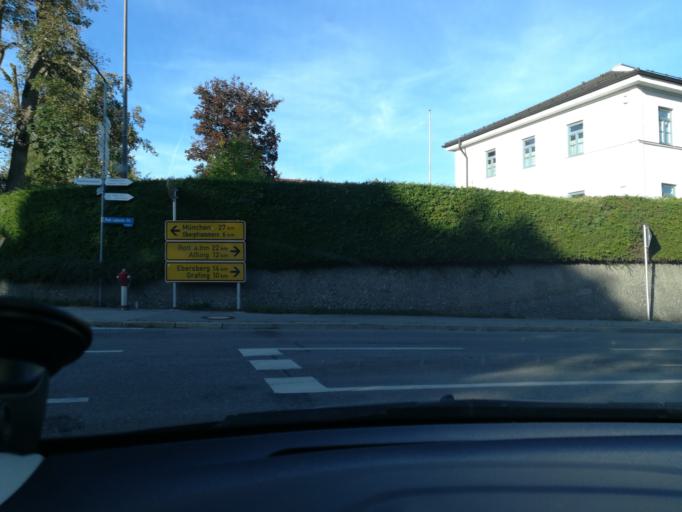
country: DE
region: Bavaria
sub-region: Upper Bavaria
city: Glonn
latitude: 47.9871
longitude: 11.8673
